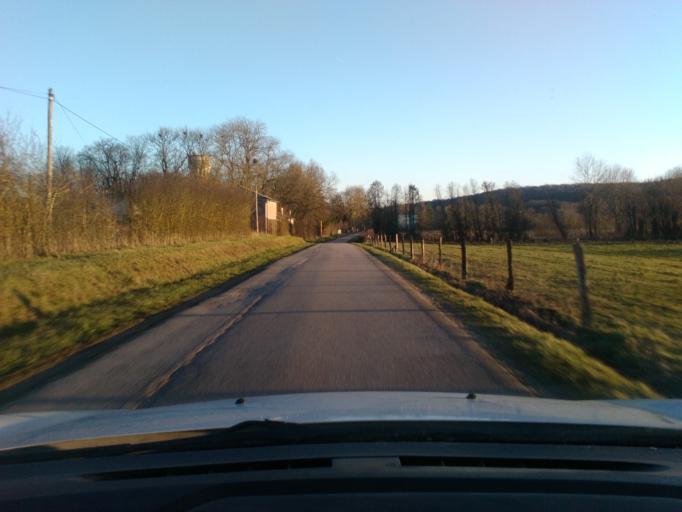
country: FR
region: Lorraine
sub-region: Departement des Vosges
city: Mirecourt
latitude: 48.2924
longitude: 6.1055
